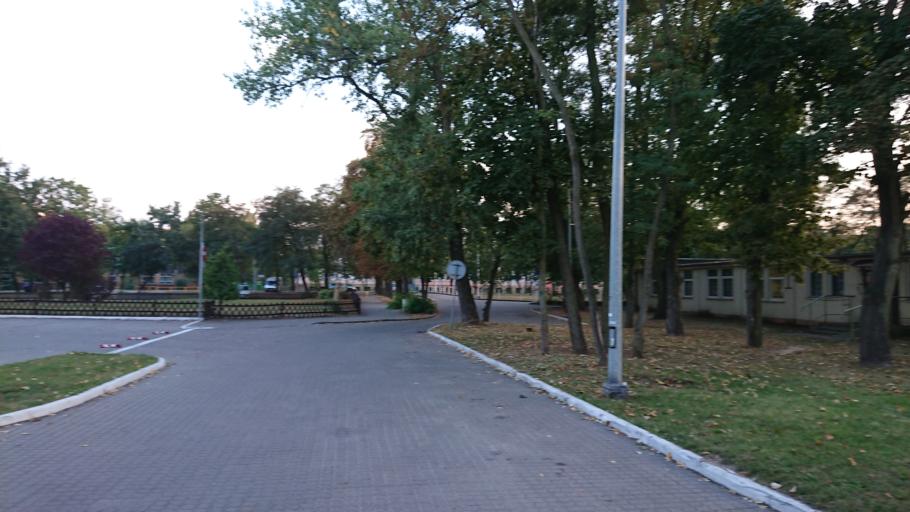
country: PL
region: Kujawsko-Pomorskie
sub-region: Powiat inowroclawski
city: Inowroclaw
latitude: 52.7901
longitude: 18.2484
